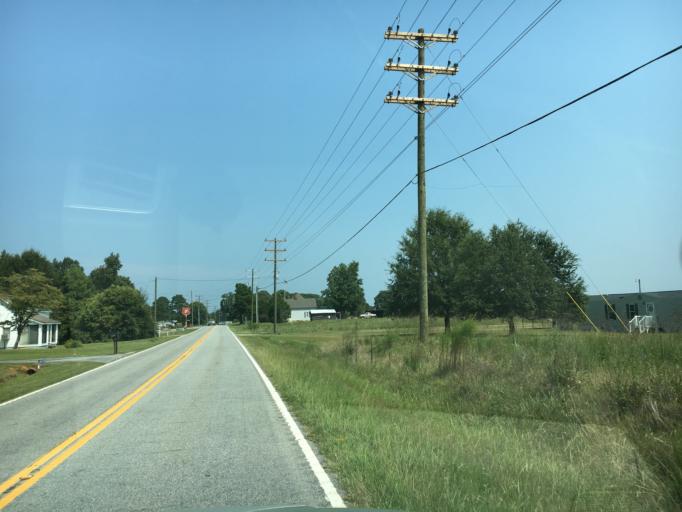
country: US
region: South Carolina
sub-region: Spartanburg County
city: Boiling Springs
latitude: 35.0631
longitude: -81.9334
